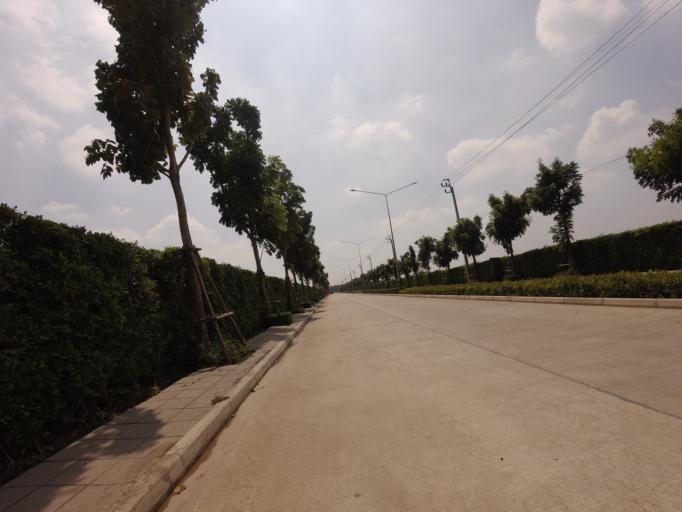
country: TH
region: Bangkok
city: Saphan Sung
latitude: 13.7530
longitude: 100.6707
